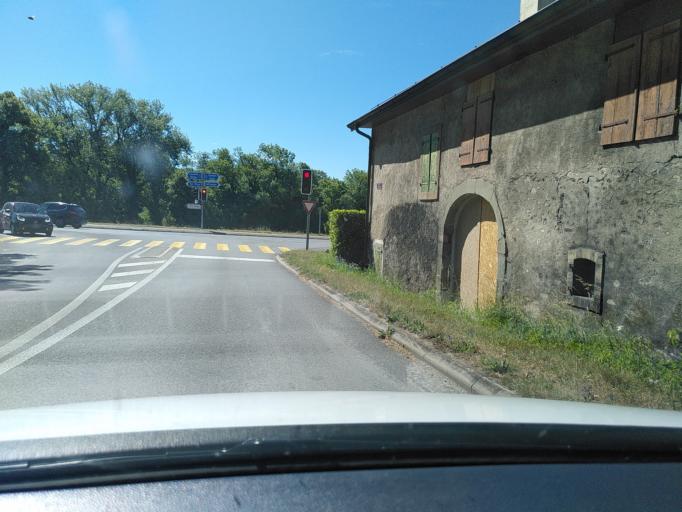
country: CH
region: Vaud
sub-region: Morges District
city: Aubonne
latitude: 46.4735
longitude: 6.4059
